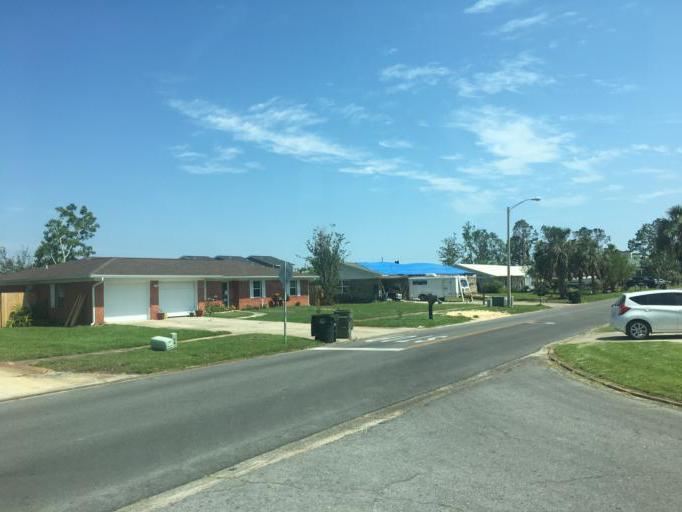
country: US
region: Florida
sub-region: Bay County
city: Lynn Haven
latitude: 30.2207
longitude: -85.6516
